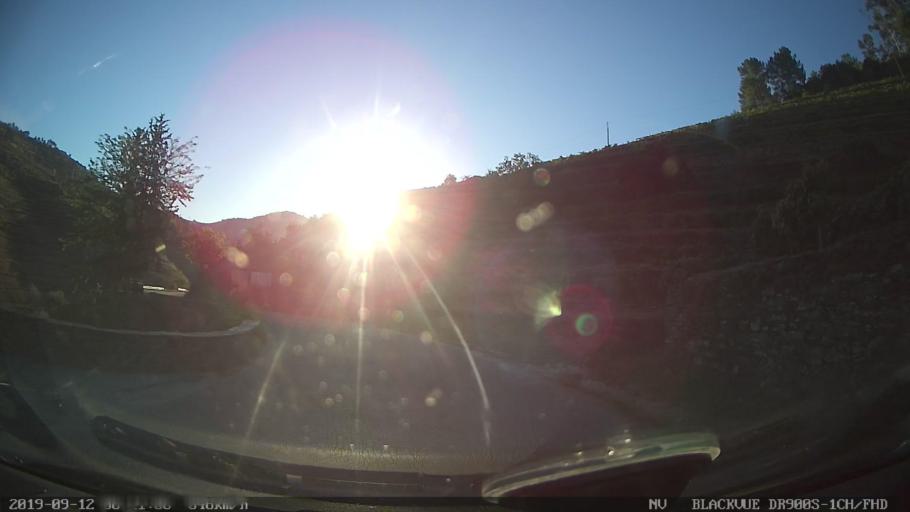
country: PT
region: Vila Real
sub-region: Sabrosa
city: Vilela
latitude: 41.1974
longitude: -7.5562
